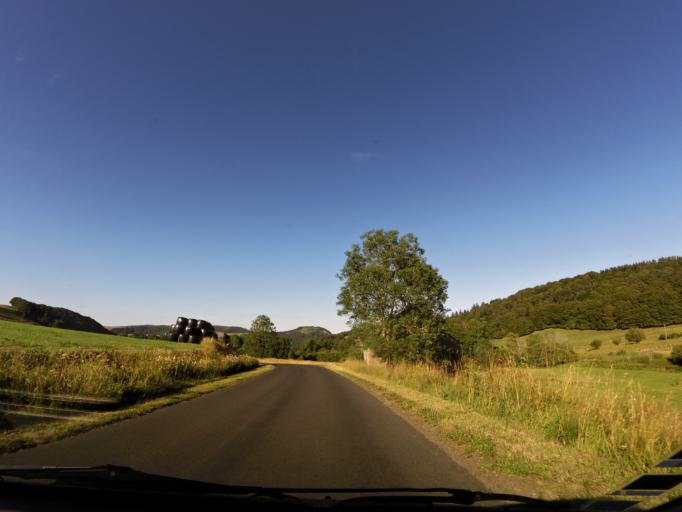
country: FR
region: Auvergne
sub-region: Departement du Puy-de-Dome
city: Mont-Dore
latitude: 45.4309
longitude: 2.9111
